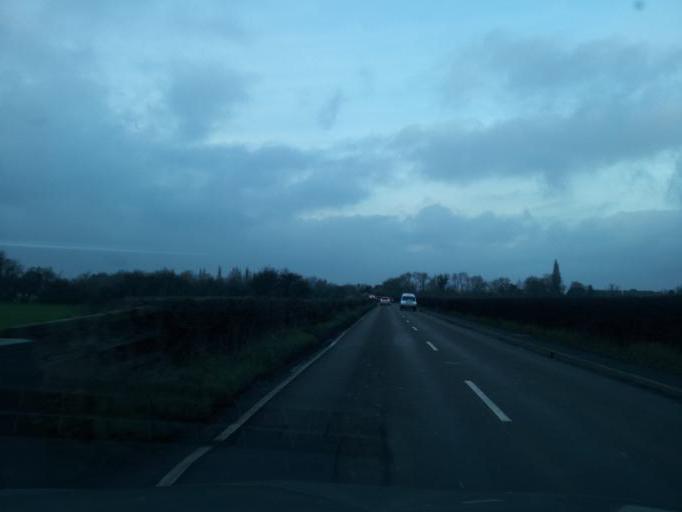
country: GB
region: England
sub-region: Derbyshire
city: Repton
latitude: 52.8457
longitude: -1.5593
